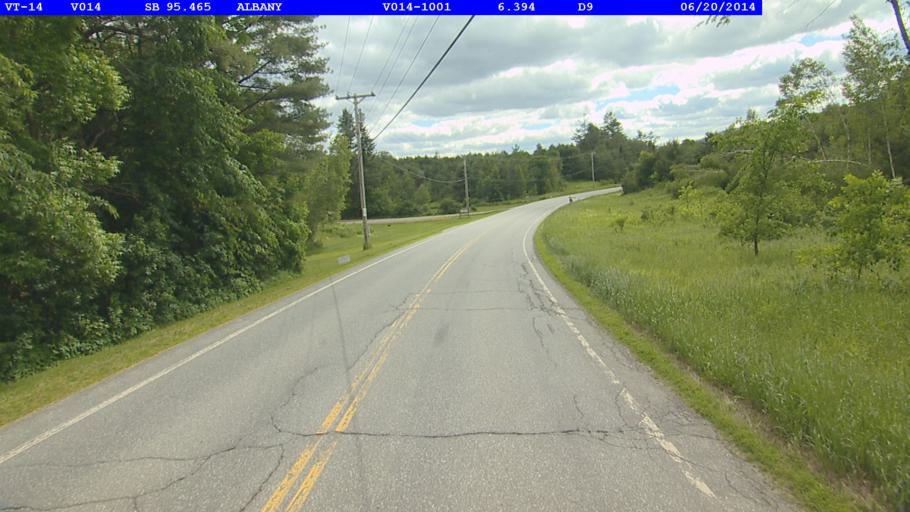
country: US
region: Vermont
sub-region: Orleans County
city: Newport
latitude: 44.7732
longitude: -72.3218
